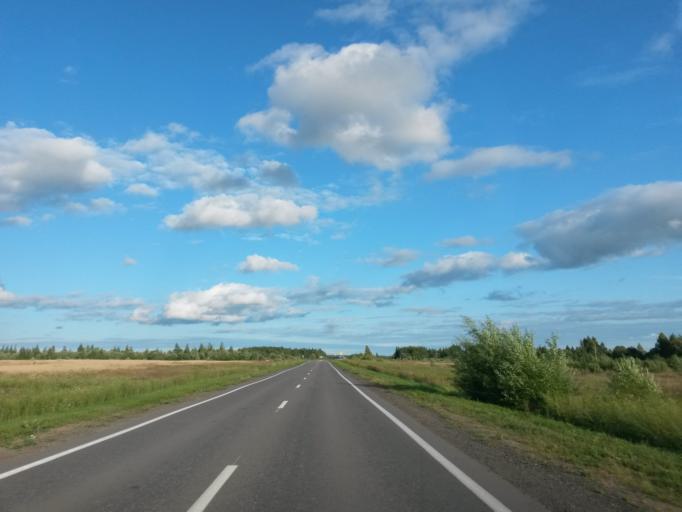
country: RU
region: Jaroslavl
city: Konstantinovskiy
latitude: 57.8725
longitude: 39.5922
